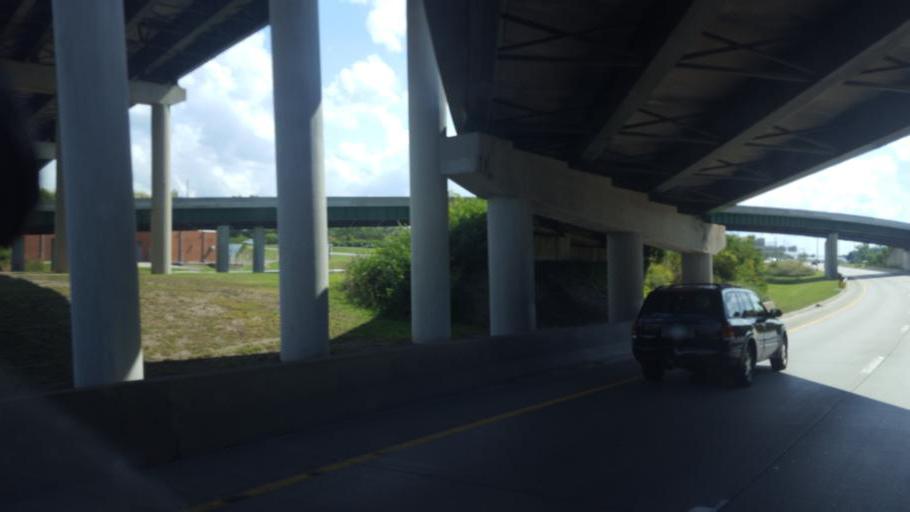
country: US
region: Ohio
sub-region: Franklin County
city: Columbus
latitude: 39.9504
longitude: -83.0172
